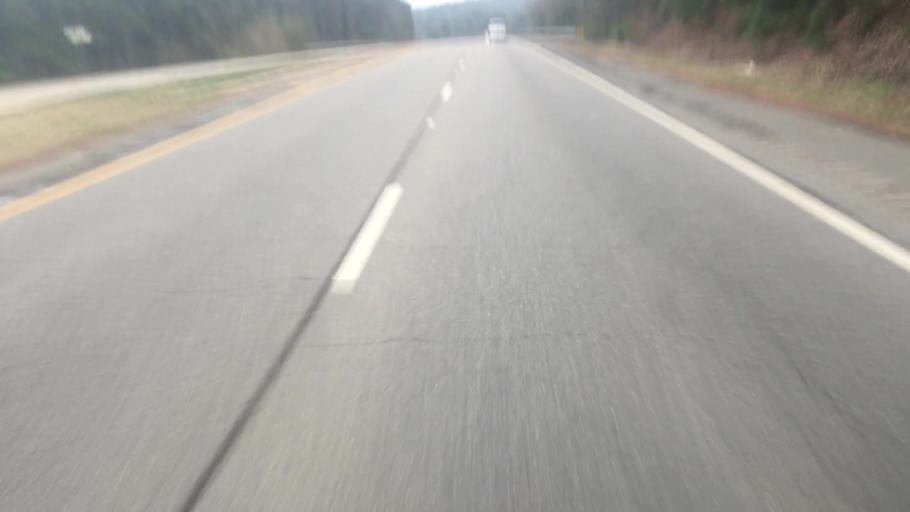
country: US
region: Alabama
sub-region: Walker County
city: Sumiton
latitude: 33.7528
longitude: -87.0604
